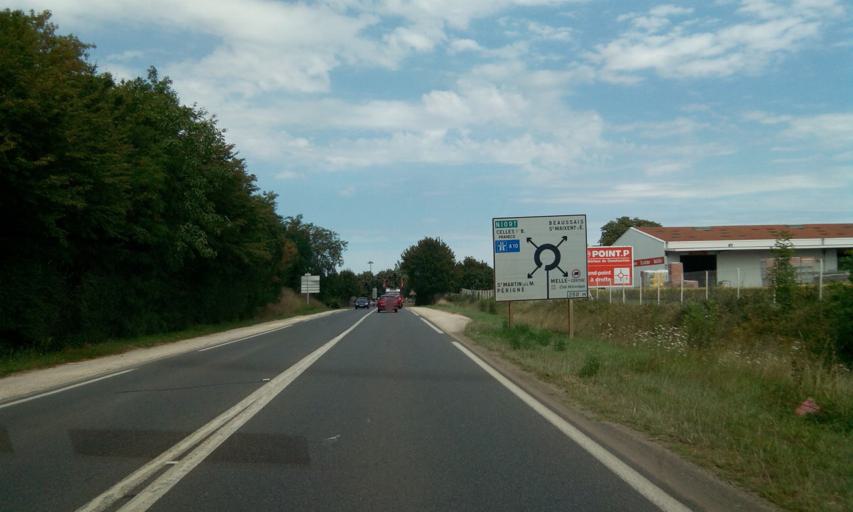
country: FR
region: Poitou-Charentes
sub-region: Departement des Deux-Sevres
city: Melle
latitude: 46.2222
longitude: -0.1553
